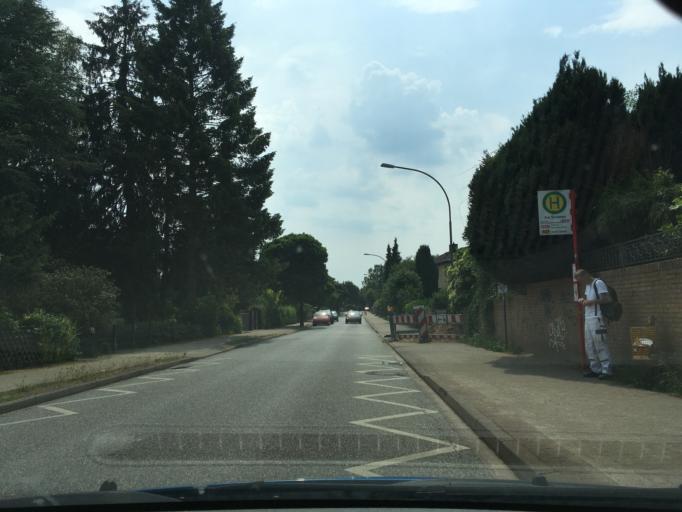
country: DE
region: Lower Saxony
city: Buchholz in der Nordheide
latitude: 53.3347
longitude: 9.8868
